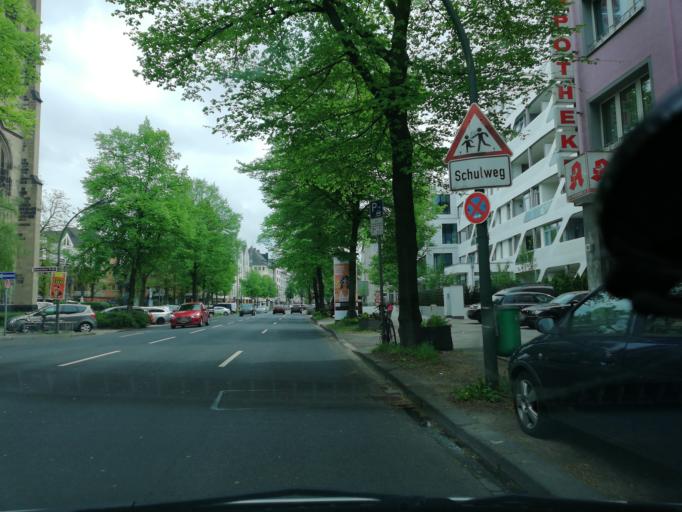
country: DE
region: North Rhine-Westphalia
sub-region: Regierungsbezirk Dusseldorf
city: Dusseldorf
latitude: 51.2469
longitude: 6.7782
